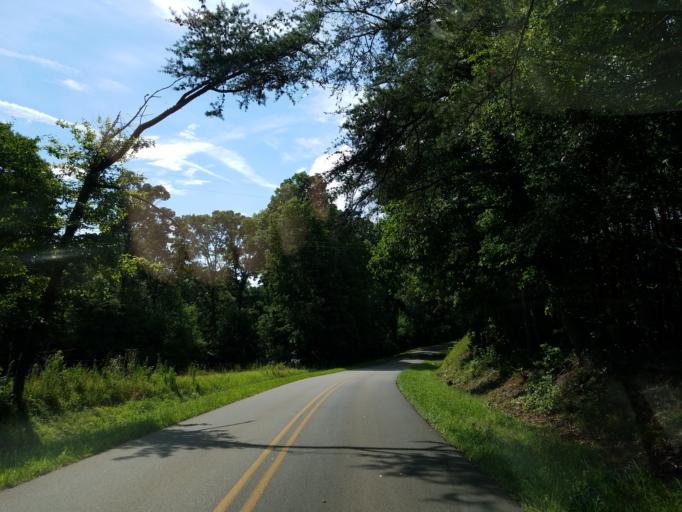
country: US
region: Georgia
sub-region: Pickens County
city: Nelson
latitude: 34.4017
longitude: -84.3825
